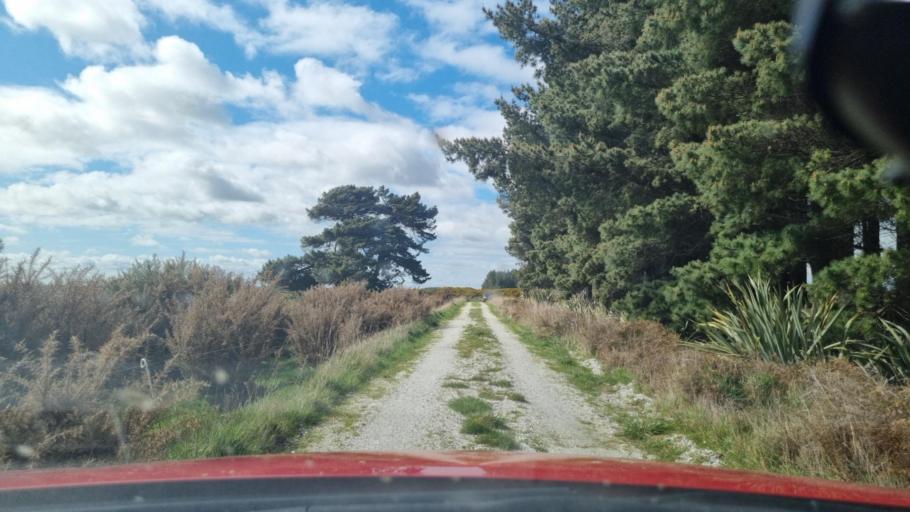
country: NZ
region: Southland
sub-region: Invercargill City
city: Invercargill
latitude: -46.4919
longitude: 168.4442
